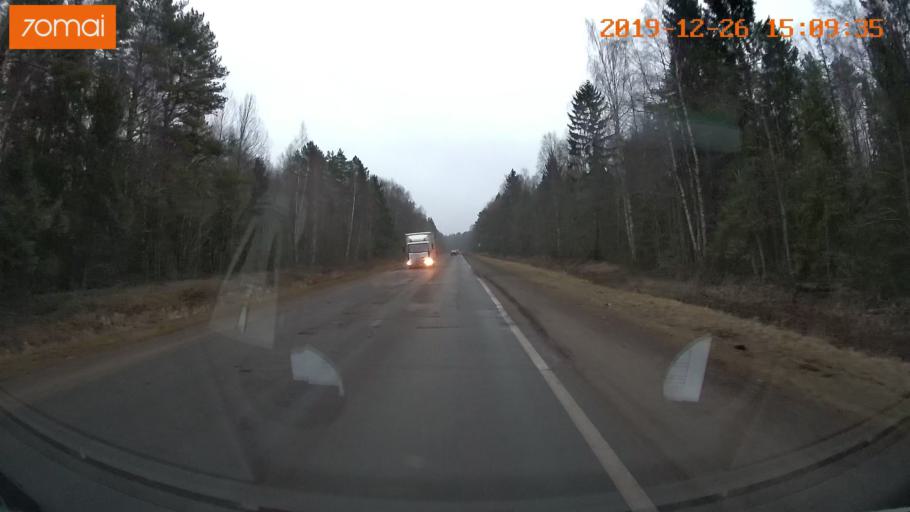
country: RU
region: Jaroslavl
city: Rybinsk
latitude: 58.1477
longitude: 38.8425
